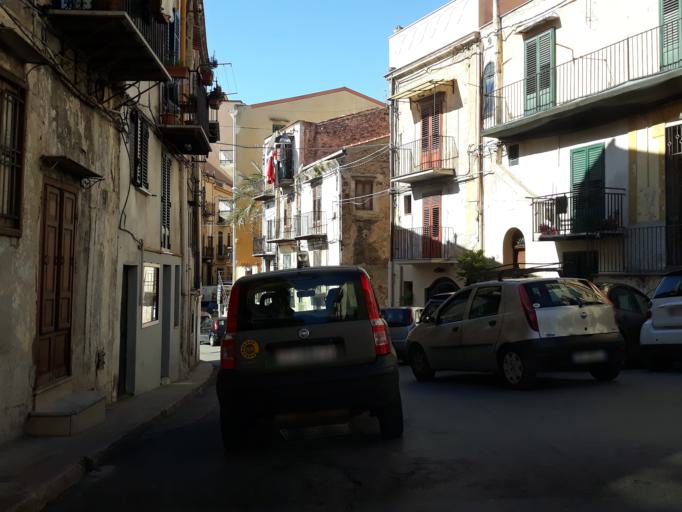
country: IT
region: Sicily
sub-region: Palermo
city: Monreale
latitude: 38.0811
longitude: 13.2882
